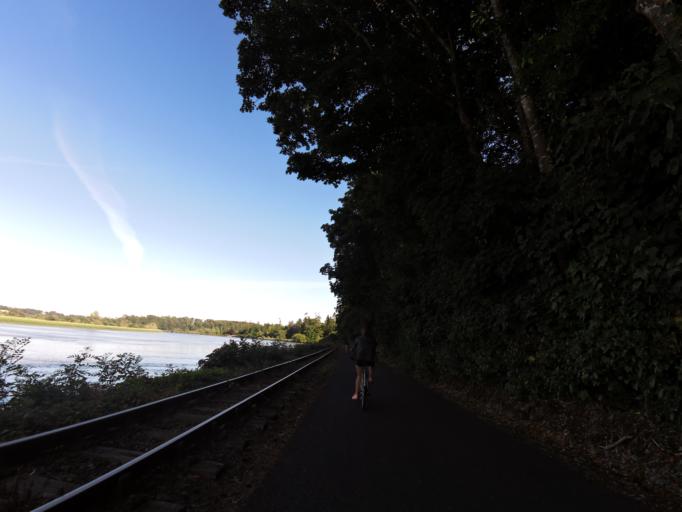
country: IE
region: Leinster
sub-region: Kilkenny
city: Mooncoin
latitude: 52.2444
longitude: -7.2254
